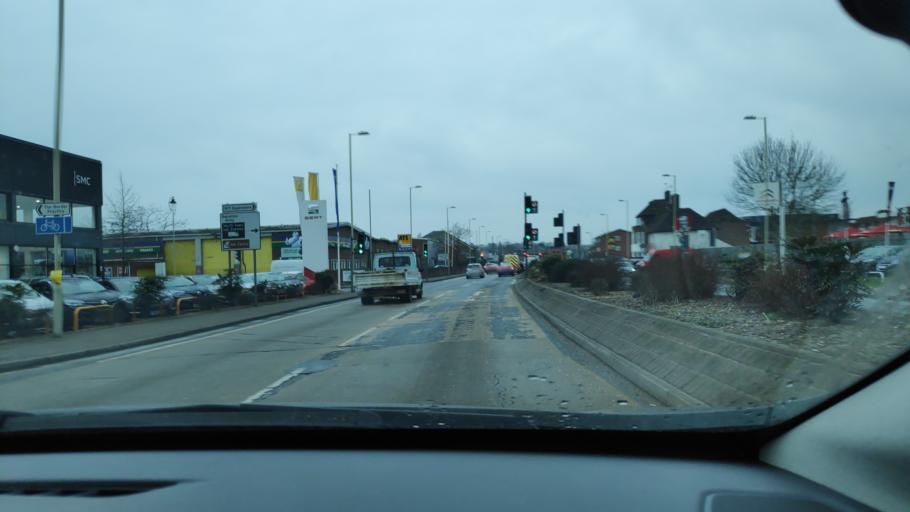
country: GB
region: England
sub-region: Surrey
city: Seale
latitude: 51.2417
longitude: -0.7384
